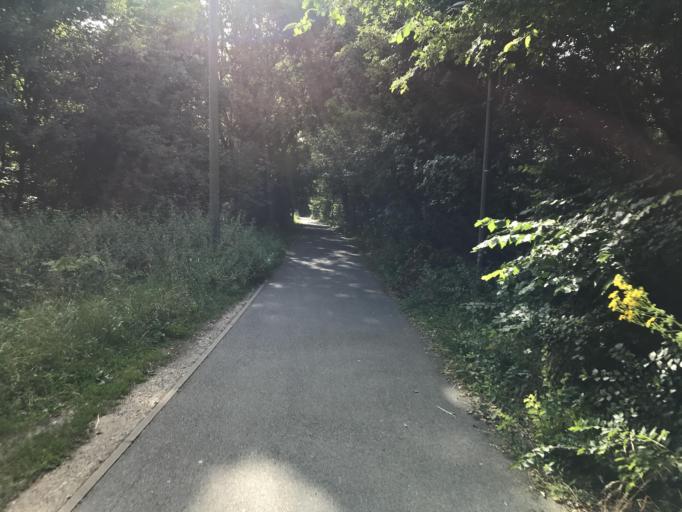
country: FR
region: Ile-de-France
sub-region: Departement de l'Essonne
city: Villebon-sur-Yvette
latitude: 48.7086
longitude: 2.2194
